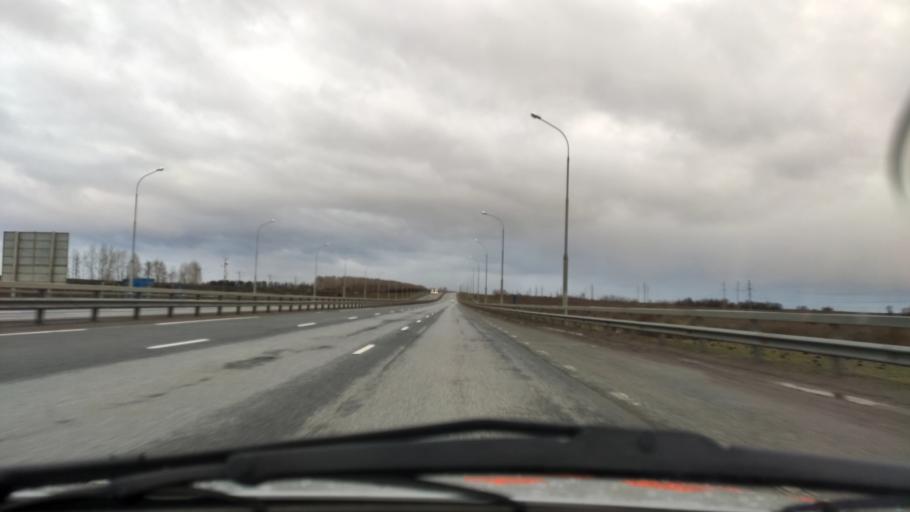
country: RU
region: Bashkortostan
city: Kabakovo
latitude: 54.6641
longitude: 56.1487
